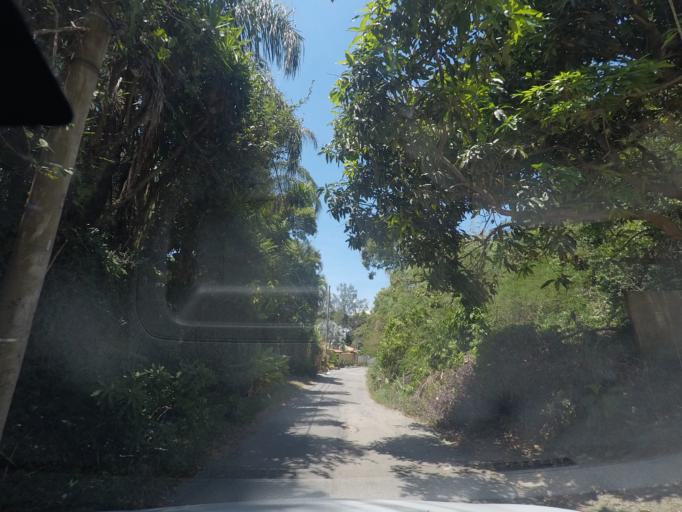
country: BR
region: Rio de Janeiro
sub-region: Niteroi
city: Niteroi
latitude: -22.9681
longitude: -43.0394
